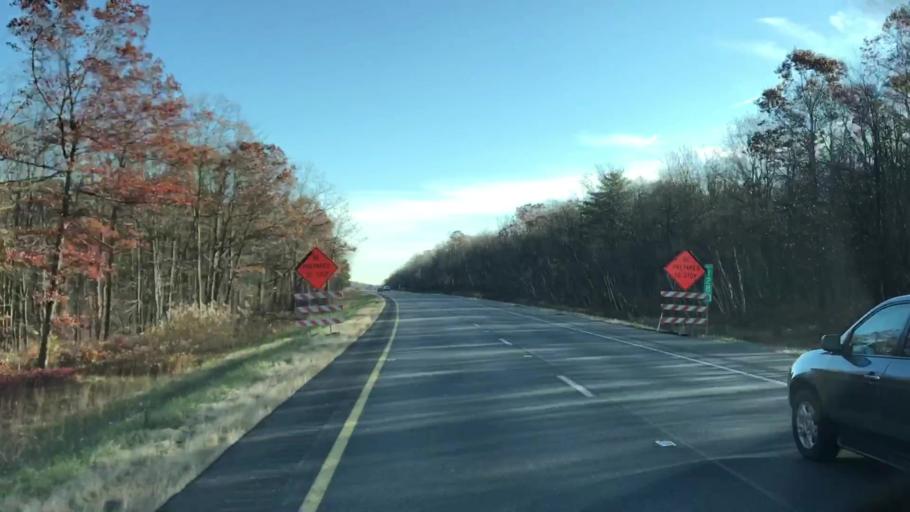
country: US
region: Pennsylvania
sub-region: Schuylkill County
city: Mahanoy City
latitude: 40.7880
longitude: -76.1460
